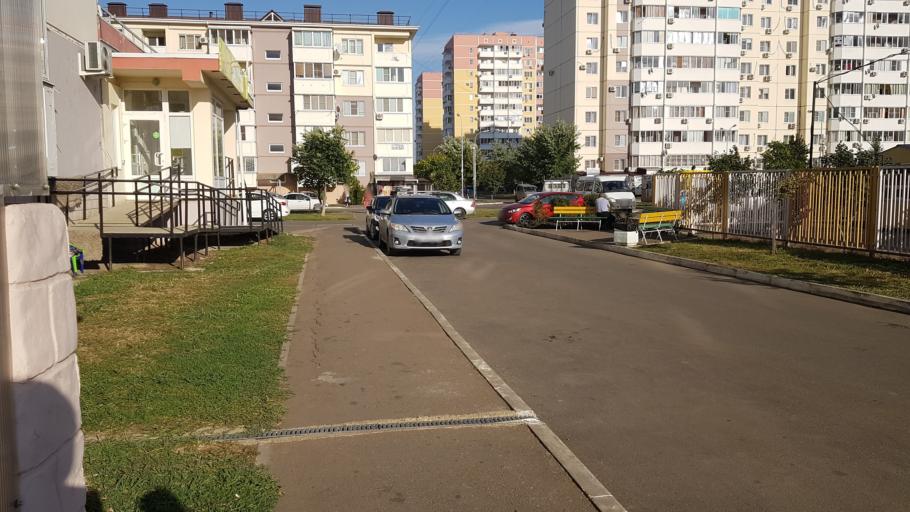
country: RU
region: Krasnodarskiy
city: Novotitarovskaya
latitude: 45.1442
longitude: 38.9935
